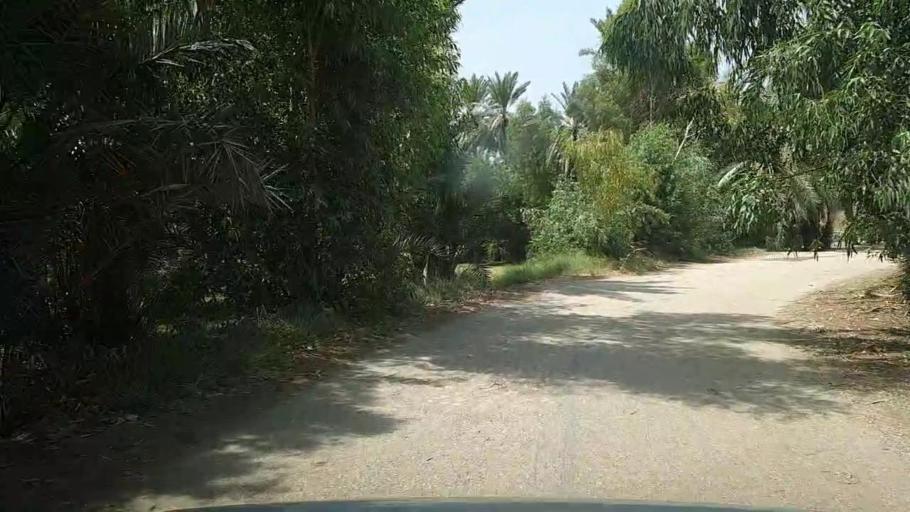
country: PK
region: Sindh
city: Pano Aqil
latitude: 27.8539
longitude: 69.1340
